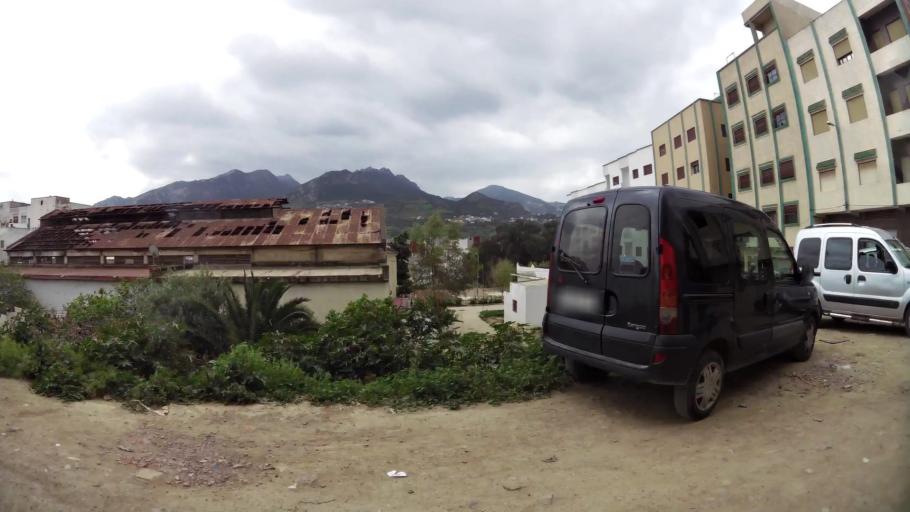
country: MA
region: Tanger-Tetouan
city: Tetouan
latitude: 35.5658
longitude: -5.3953
